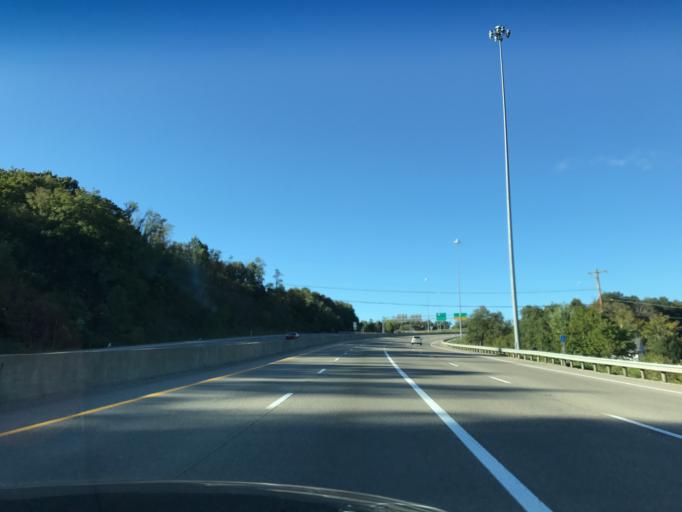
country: US
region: Ohio
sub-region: Washington County
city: Belpre
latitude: 39.2612
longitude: -81.5759
